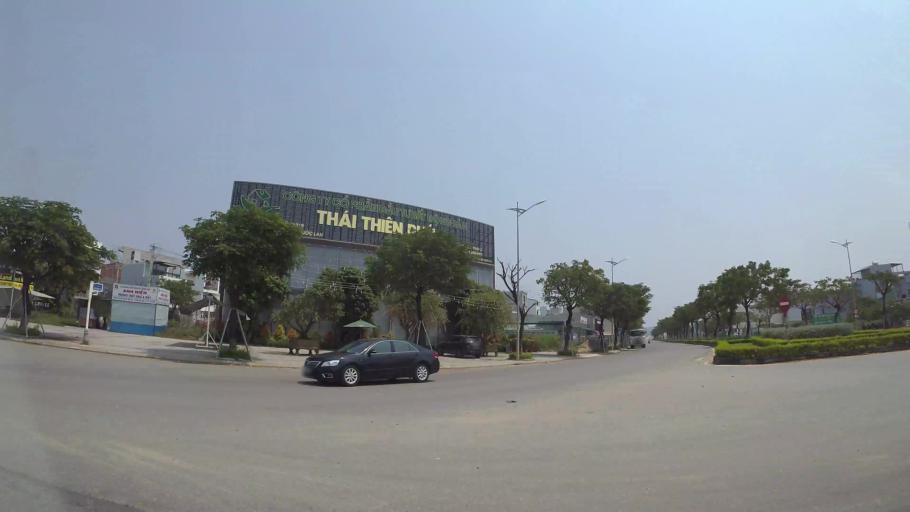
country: VN
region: Da Nang
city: Ngu Hanh Son
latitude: 16.0186
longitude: 108.2304
